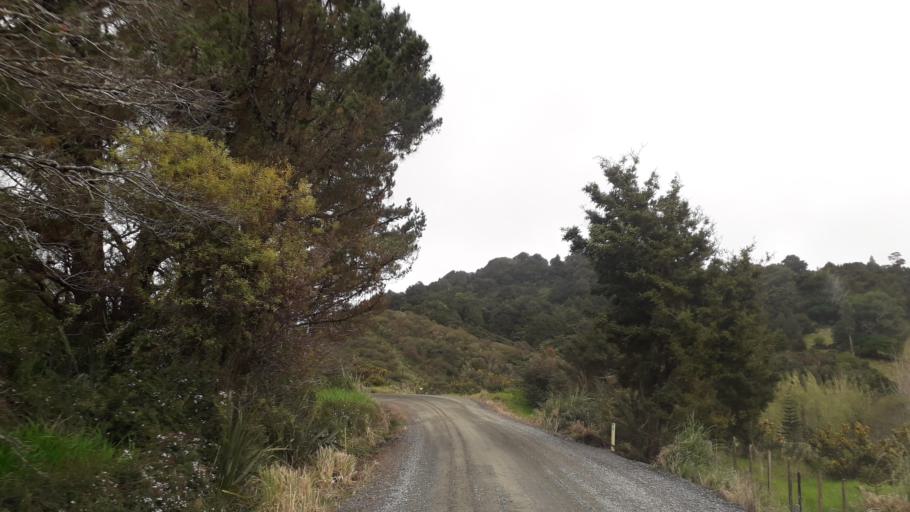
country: NZ
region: Northland
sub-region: Far North District
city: Kerikeri
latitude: -35.1216
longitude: 173.7477
